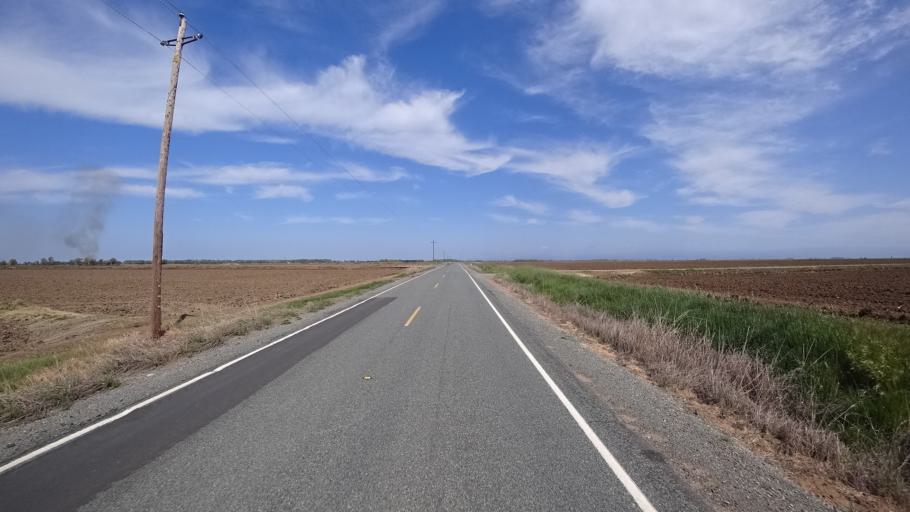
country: US
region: California
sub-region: Butte County
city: Durham
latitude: 39.4989
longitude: -121.8574
